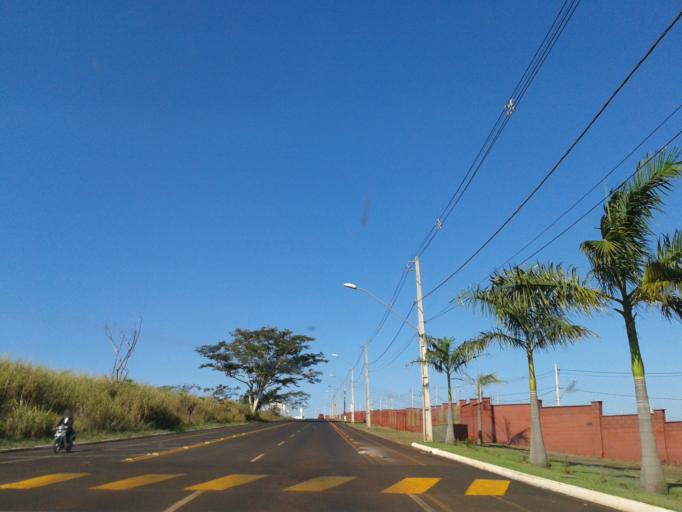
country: BR
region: Goias
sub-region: Itumbiara
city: Itumbiara
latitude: -18.4275
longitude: -49.1999
